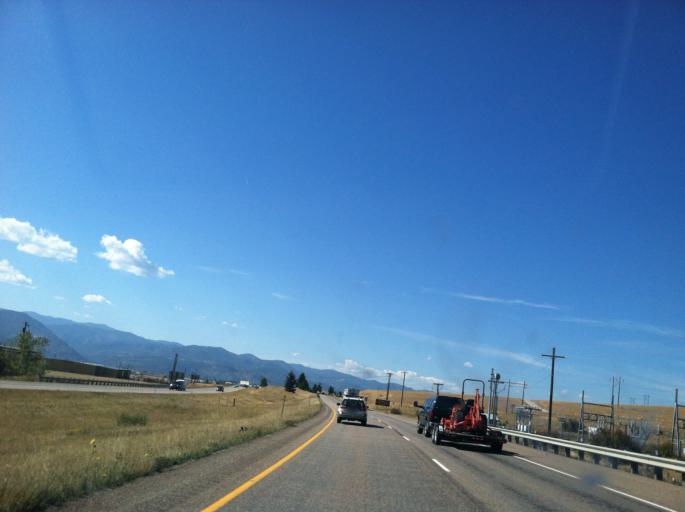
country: US
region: Montana
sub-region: Missoula County
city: Orchard Homes
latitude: 46.9378
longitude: -114.0983
